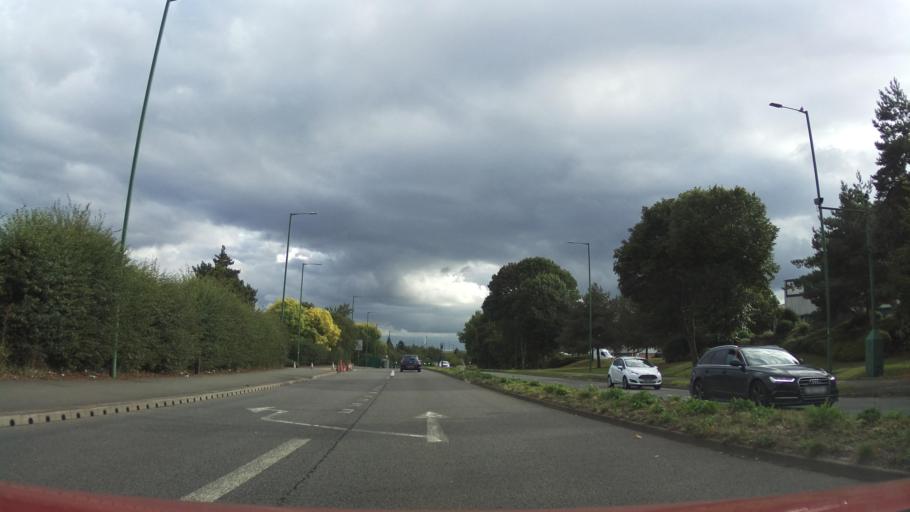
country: GB
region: England
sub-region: Solihull
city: Bickenhill
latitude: 52.4574
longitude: -1.7280
